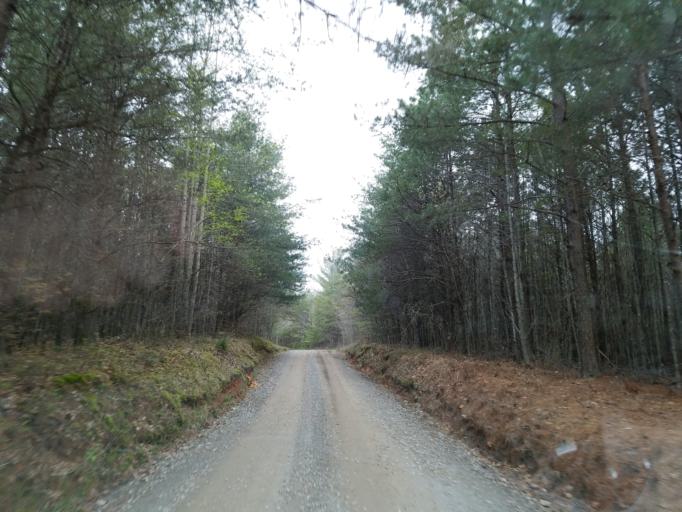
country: US
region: Georgia
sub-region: Gilmer County
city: Ellijay
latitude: 34.6540
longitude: -84.2983
